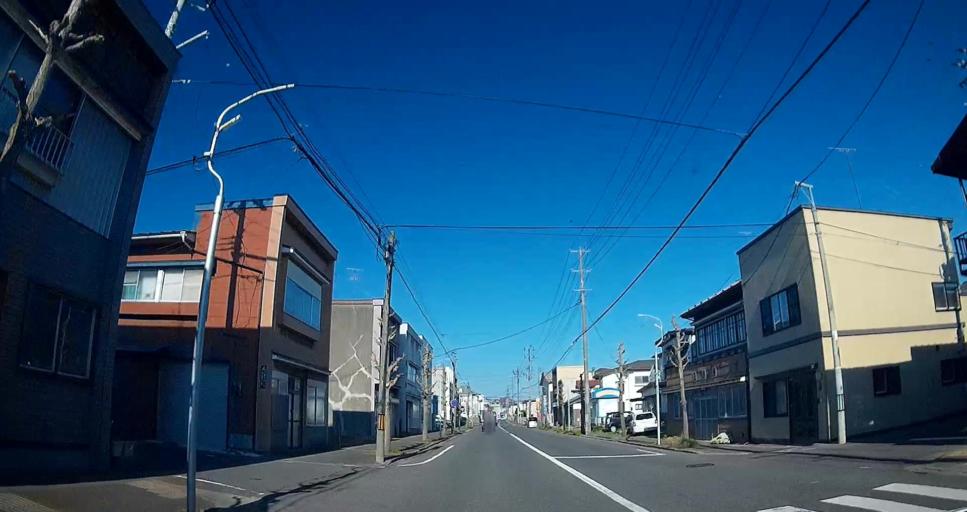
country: JP
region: Aomori
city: Hachinohe
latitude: 40.5226
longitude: 141.5412
